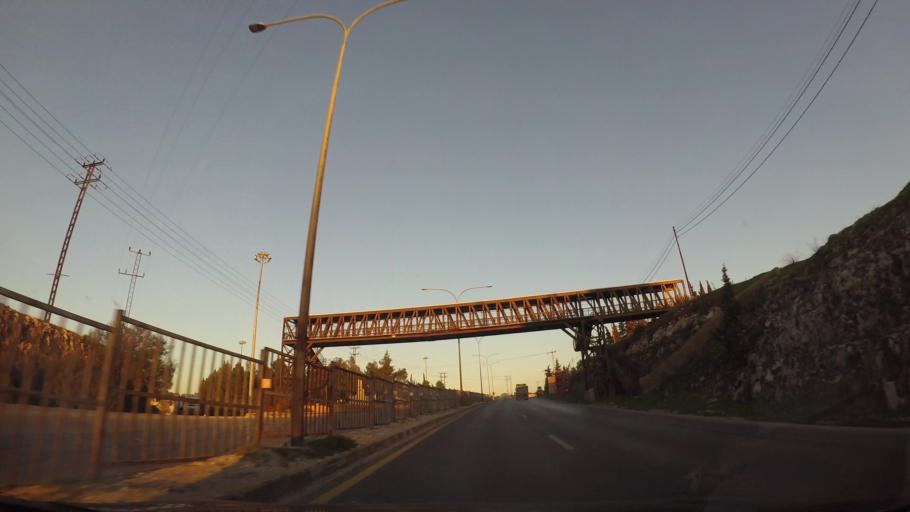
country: JO
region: Amman
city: Umm as Summaq
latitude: 31.8634
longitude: 35.8202
